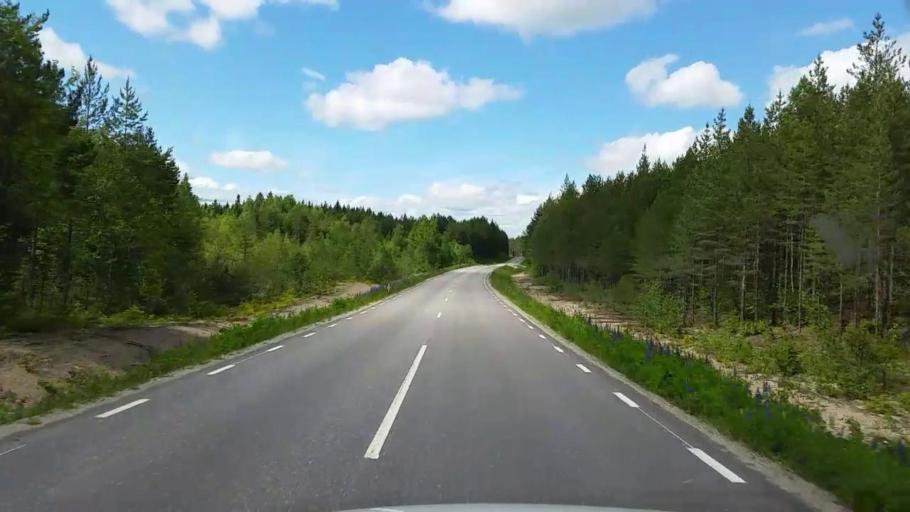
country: SE
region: Gaevleborg
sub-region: Ovanakers Kommun
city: Alfta
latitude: 61.2765
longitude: 16.1077
